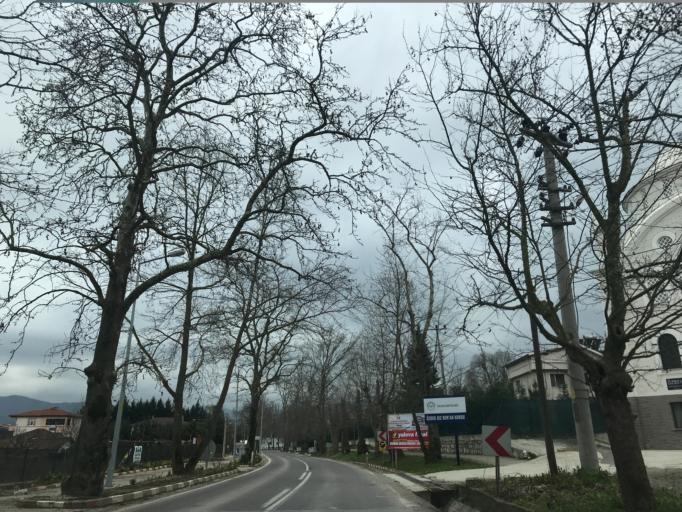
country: TR
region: Yalova
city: Kadikoy
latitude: 40.6321
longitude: 29.2239
